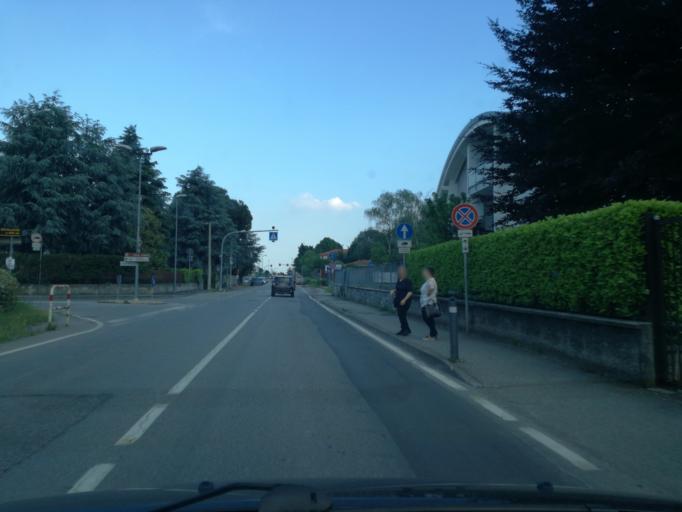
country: IT
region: Lombardy
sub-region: Provincia di Monza e Brianza
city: Cornate d'Adda
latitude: 45.6445
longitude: 9.4658
